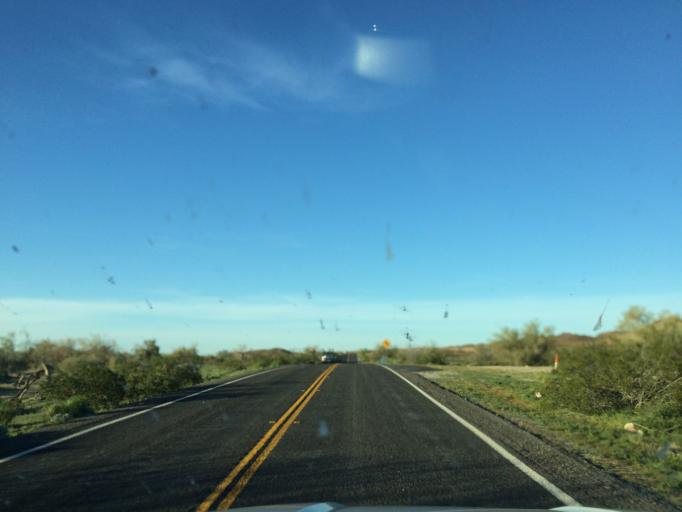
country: MX
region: Baja California
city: Los Algodones
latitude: 33.1518
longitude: -114.8704
